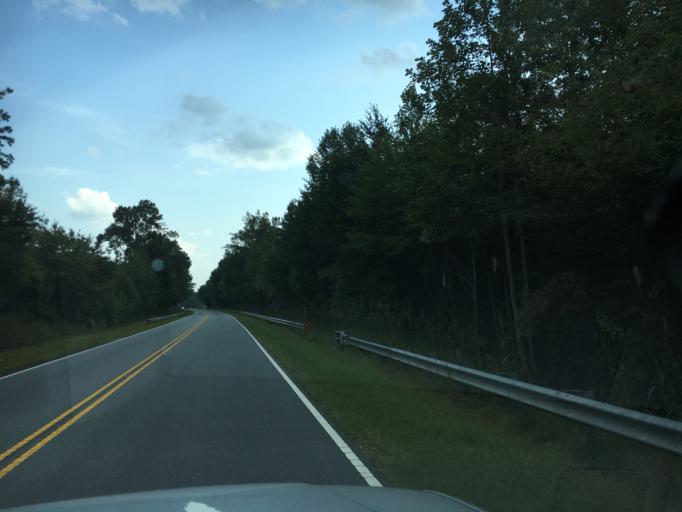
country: US
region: North Carolina
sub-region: Rutherford County
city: Rutherfordton
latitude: 35.4742
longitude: -81.9815
